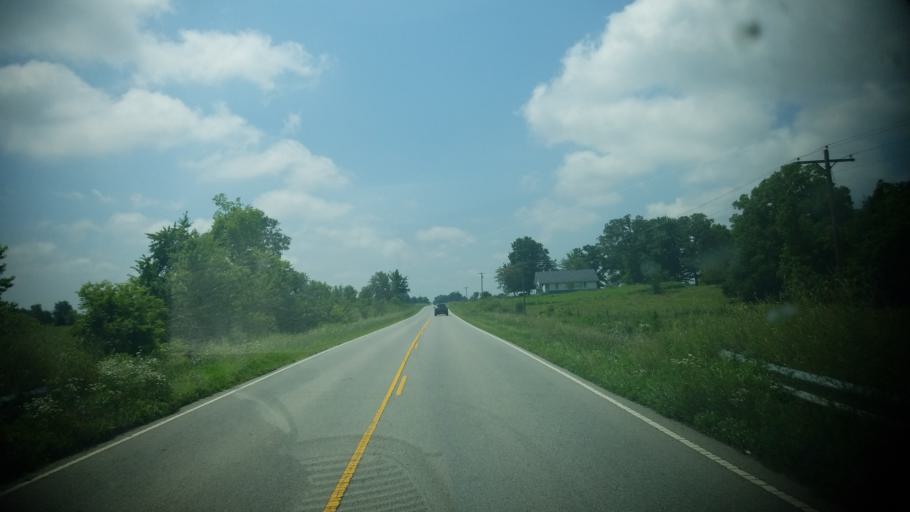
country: US
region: Illinois
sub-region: Wayne County
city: Fairfield
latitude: 38.4762
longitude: -88.3487
